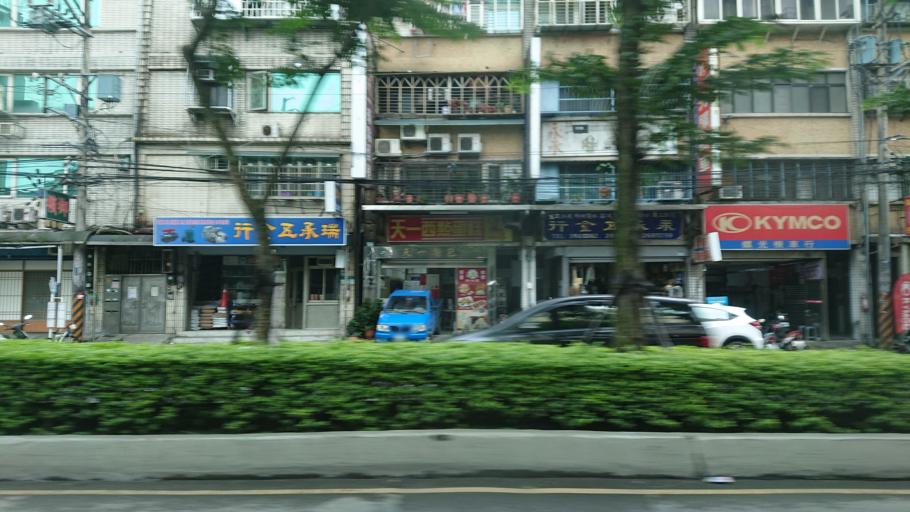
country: TW
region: Taipei
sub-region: Taipei
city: Banqiao
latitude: 24.9625
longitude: 121.4250
